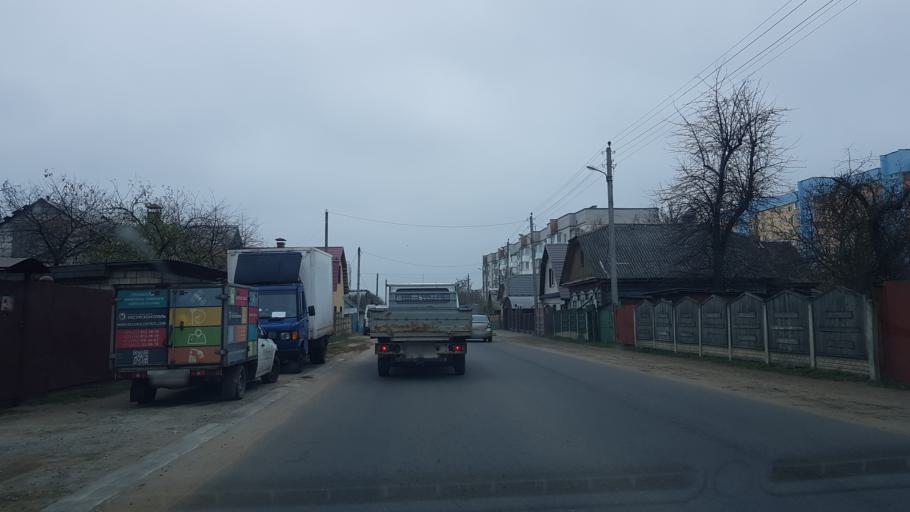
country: BY
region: Mogilev
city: Babruysk
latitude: 53.1561
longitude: 29.2293
